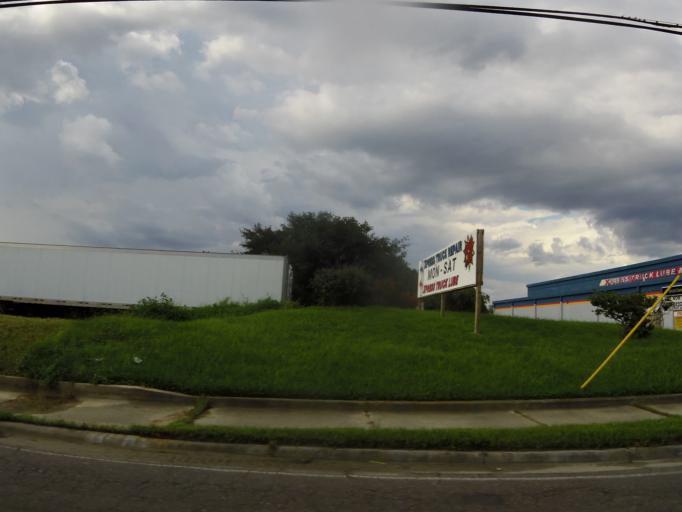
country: US
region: Florida
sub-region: Duval County
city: Jacksonville
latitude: 30.3358
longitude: -81.7509
